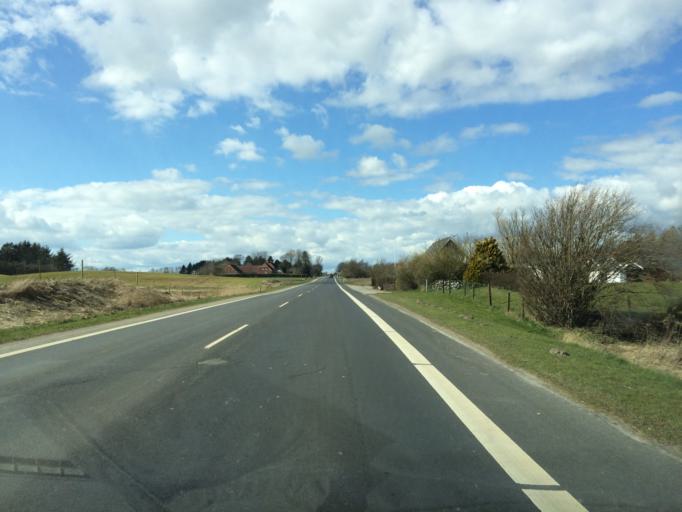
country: DK
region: South Denmark
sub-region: Assens Kommune
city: Arup
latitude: 55.4191
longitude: 10.0421
